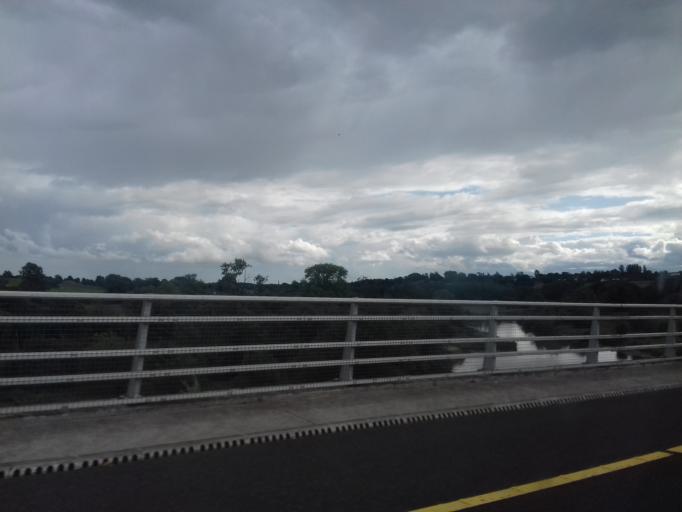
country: IE
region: Leinster
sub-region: Kilkenny
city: Thomastown
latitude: 52.6002
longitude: -7.1816
